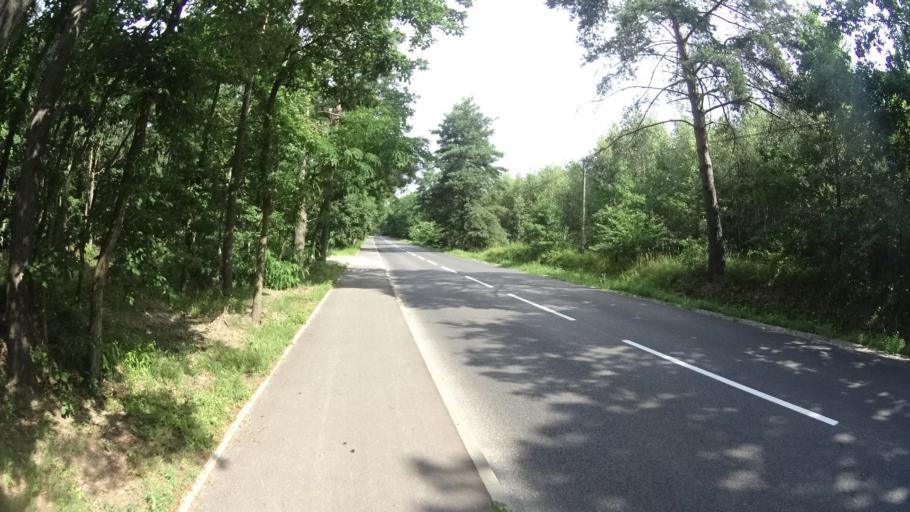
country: PL
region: Masovian Voivodeship
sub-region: Powiat piaseczynski
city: Tarczyn
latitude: 52.0265
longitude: 20.7841
